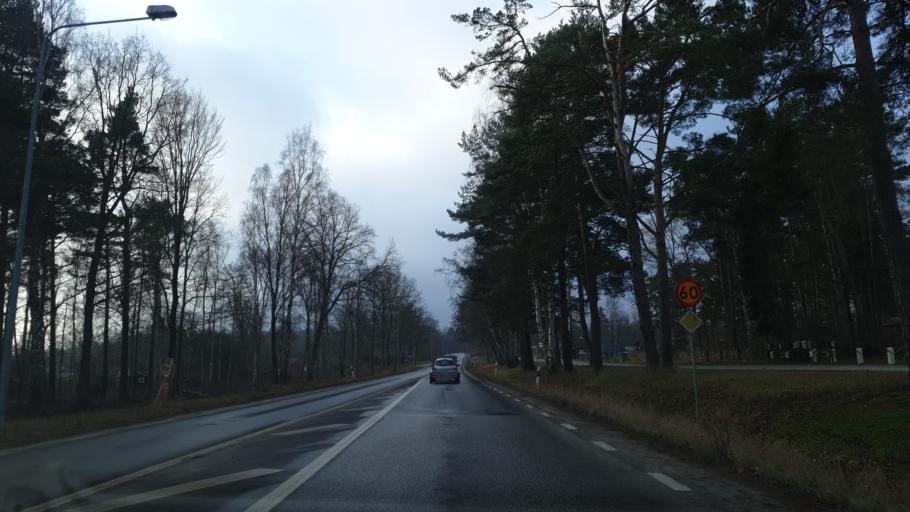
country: SE
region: Blekinge
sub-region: Karlshamns Kommun
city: Morrum
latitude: 56.1530
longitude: 14.6728
